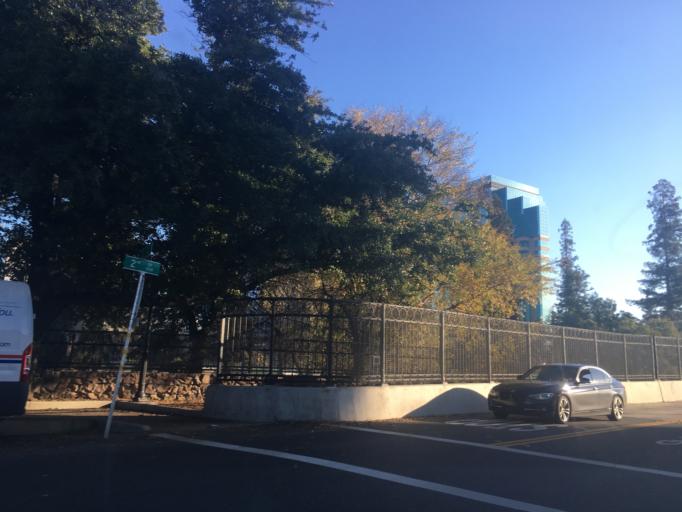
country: US
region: California
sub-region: Sacramento County
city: Sacramento
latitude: 38.5809
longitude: -121.5051
